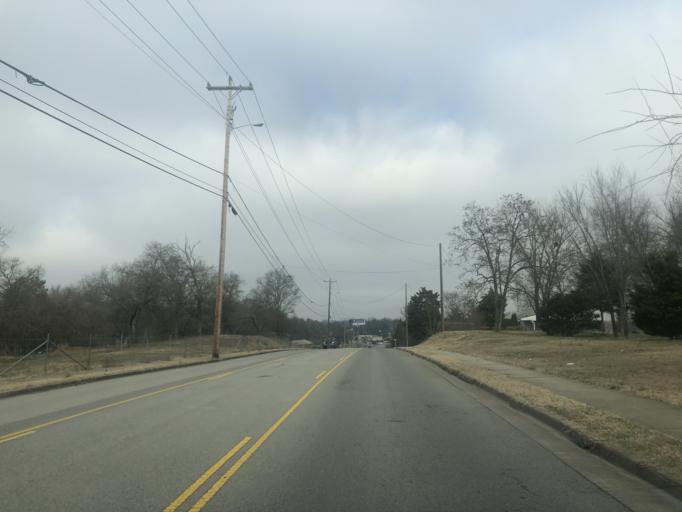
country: US
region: Tennessee
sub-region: Rutherford County
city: La Vergne
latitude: 36.0702
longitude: -86.6395
